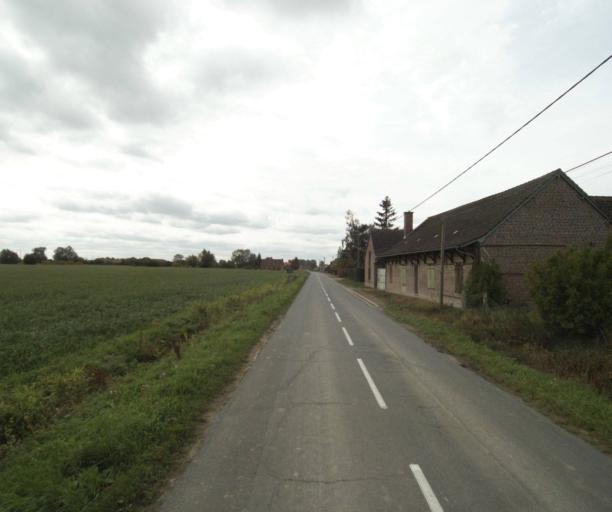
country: FR
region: Nord-Pas-de-Calais
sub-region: Departement du Nord
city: Bois-Grenier
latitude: 50.6380
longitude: 2.8940
